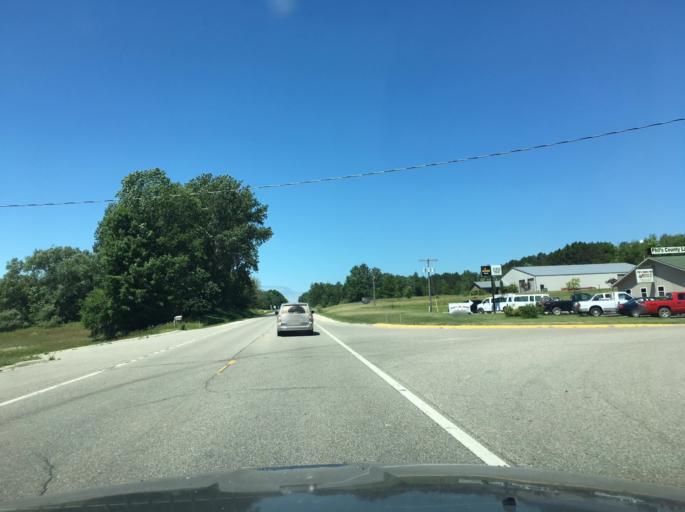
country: US
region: Michigan
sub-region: Osceola County
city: Reed City
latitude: 43.8876
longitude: -85.5561
